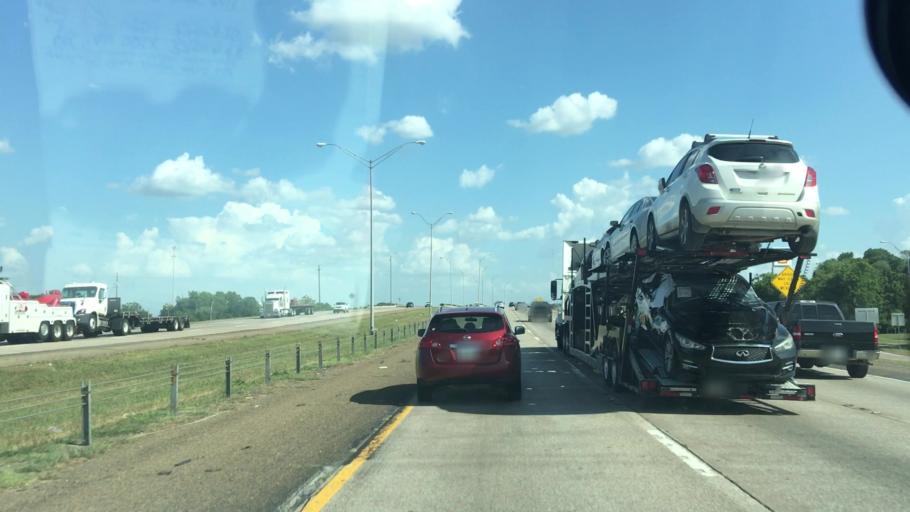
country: US
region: Texas
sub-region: Dallas County
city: Hutchins
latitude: 32.7169
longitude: -96.7586
